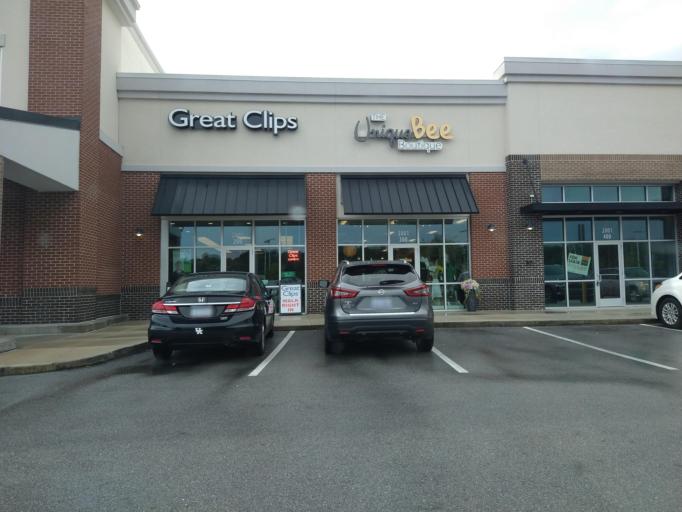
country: US
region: North Carolina
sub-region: Onslow County
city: Pumpkin Center
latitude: 34.7960
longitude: -77.4076
